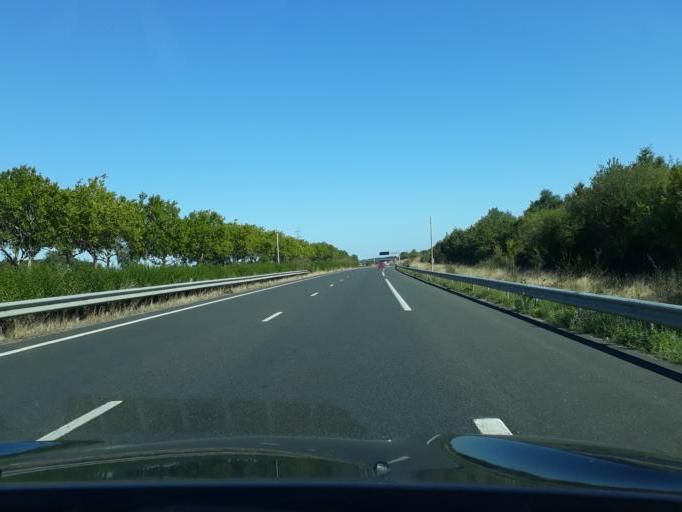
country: FR
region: Centre
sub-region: Departement d'Indre-et-Loire
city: Artannes-sur-Indre
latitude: 47.3087
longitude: 0.5731
